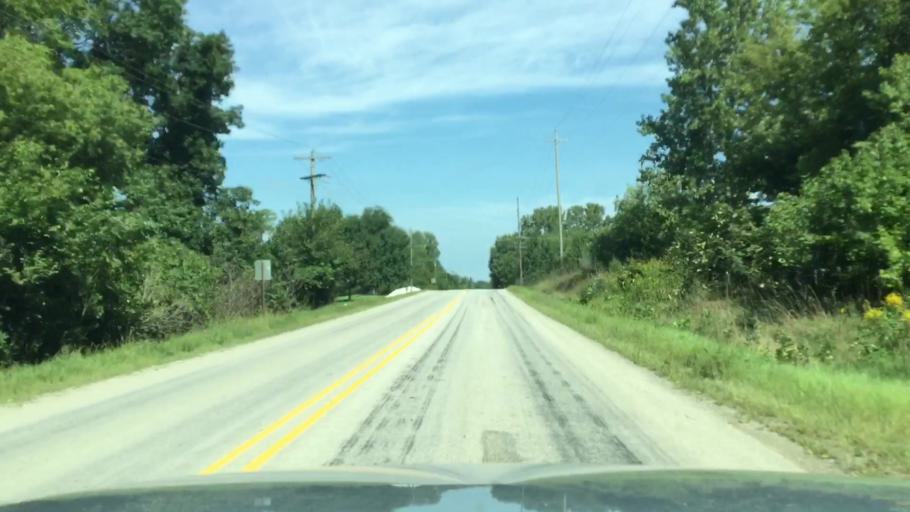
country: US
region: Michigan
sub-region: Lenawee County
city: Manitou Beach-Devils Lake
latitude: 42.0087
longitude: -84.2760
